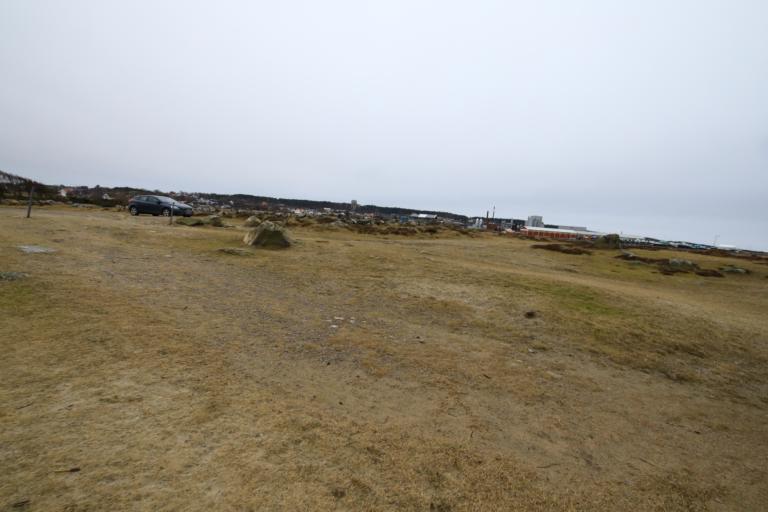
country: SE
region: Halland
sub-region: Kungsbacka Kommun
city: Frillesas
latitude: 57.2439
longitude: 12.1214
